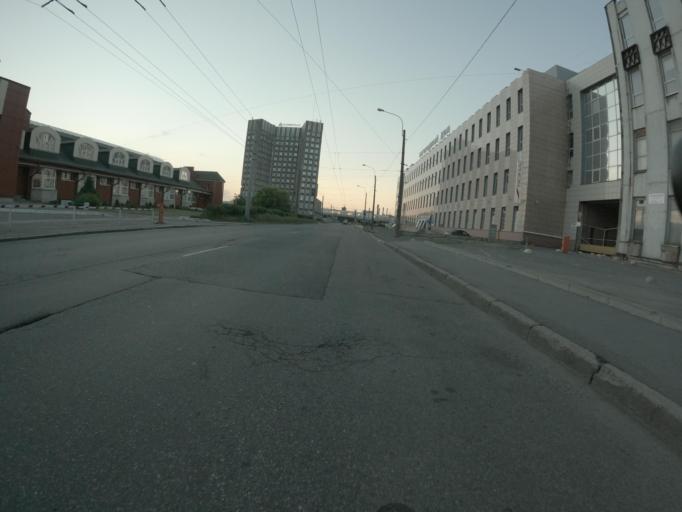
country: RU
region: St.-Petersburg
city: Avtovo
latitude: 59.8529
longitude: 30.2830
